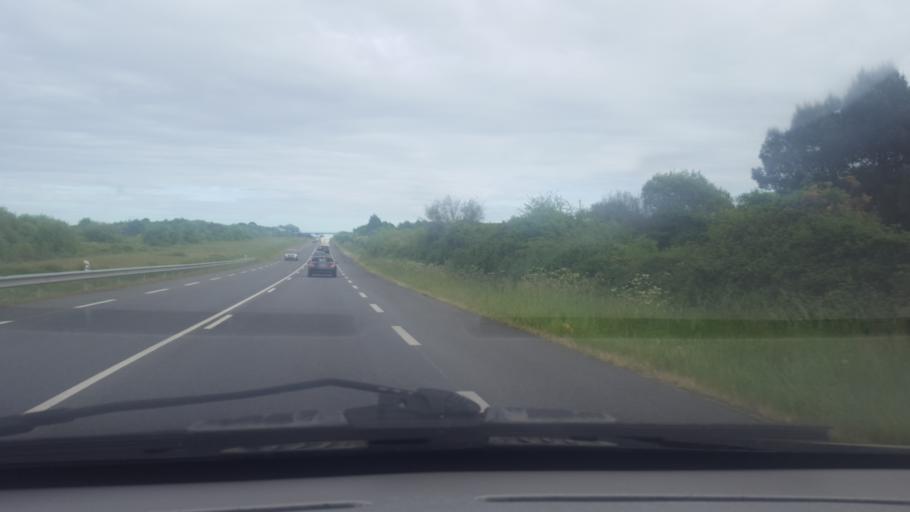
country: FR
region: Pays de la Loire
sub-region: Departement de la Loire-Atlantique
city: Les Moutiers-en-Retz
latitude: 47.0752
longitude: -2.0012
